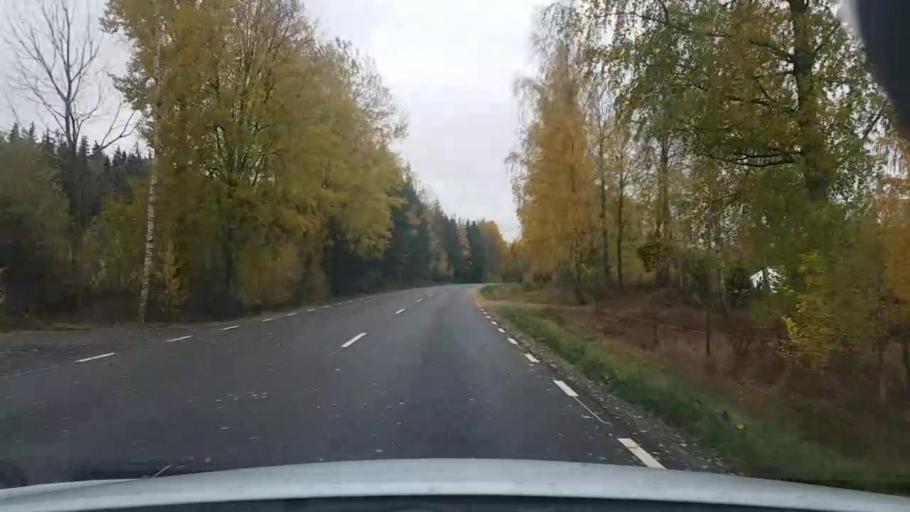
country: SE
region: OErebro
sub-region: Laxa Kommun
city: Laxa
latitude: 58.7710
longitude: 14.5344
